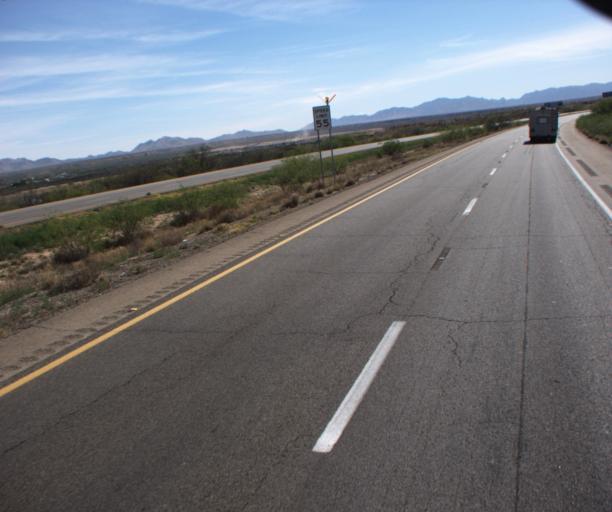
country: US
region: Arizona
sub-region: Cochise County
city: Benson
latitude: 31.9781
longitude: -110.2957
